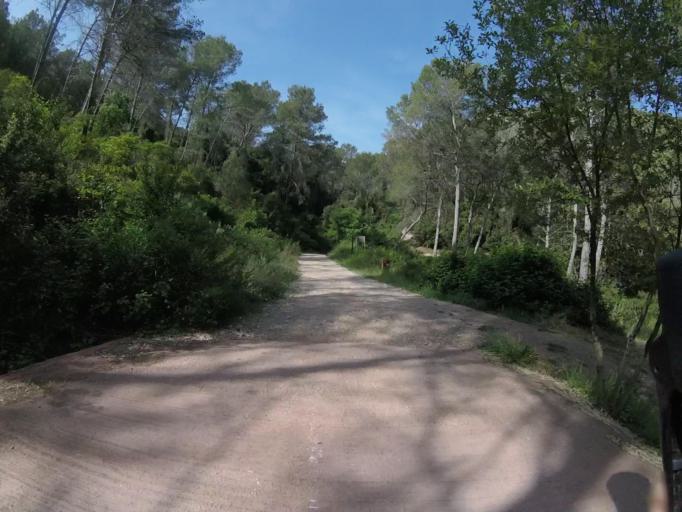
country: ES
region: Valencia
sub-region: Provincia de Castello
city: Cabanes
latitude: 40.1032
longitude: 0.0378
